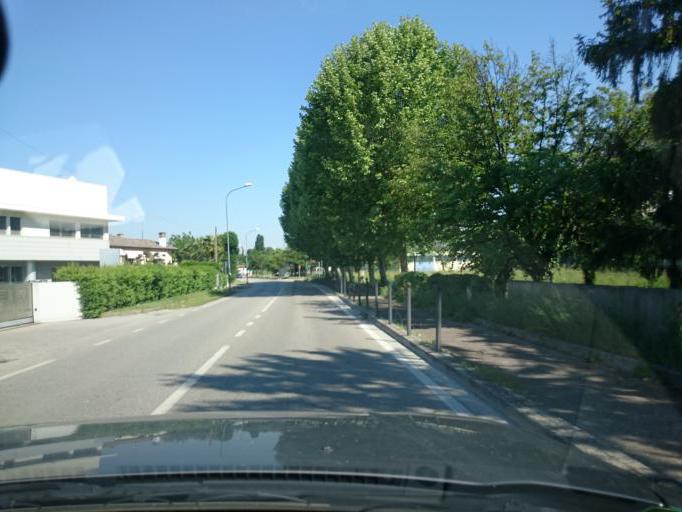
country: IT
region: Veneto
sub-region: Provincia di Venezia
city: Stra
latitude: 45.4202
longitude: 12.0151
